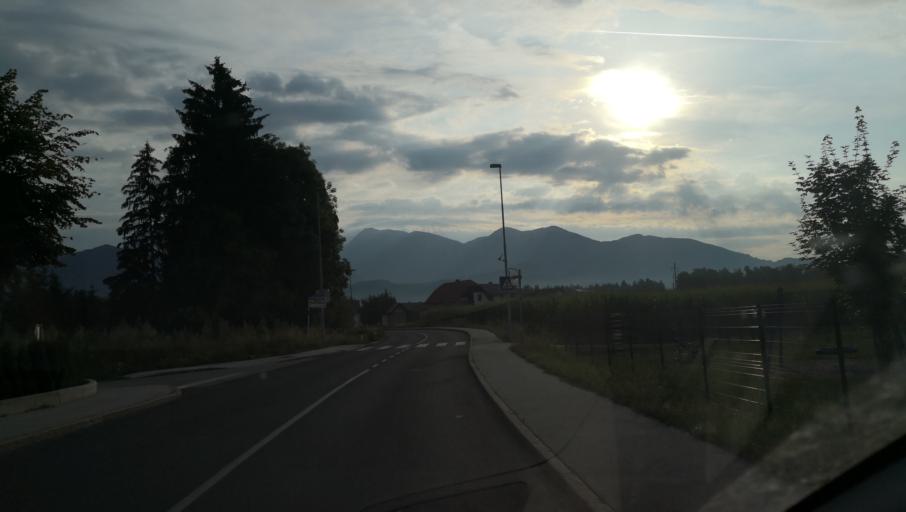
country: SI
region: Kranj
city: Britof
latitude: 46.2647
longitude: 14.3992
